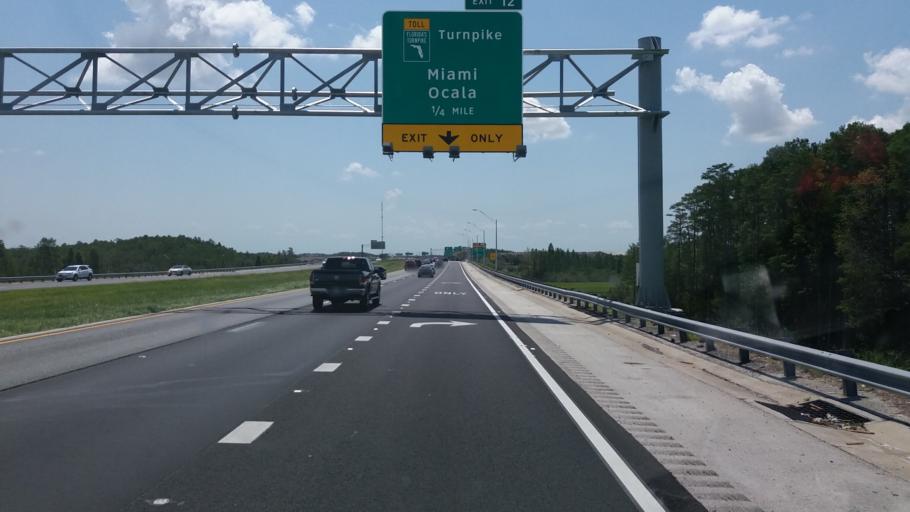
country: US
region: Florida
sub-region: Orange County
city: Hunters Creek
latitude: 28.3719
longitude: -81.4030
